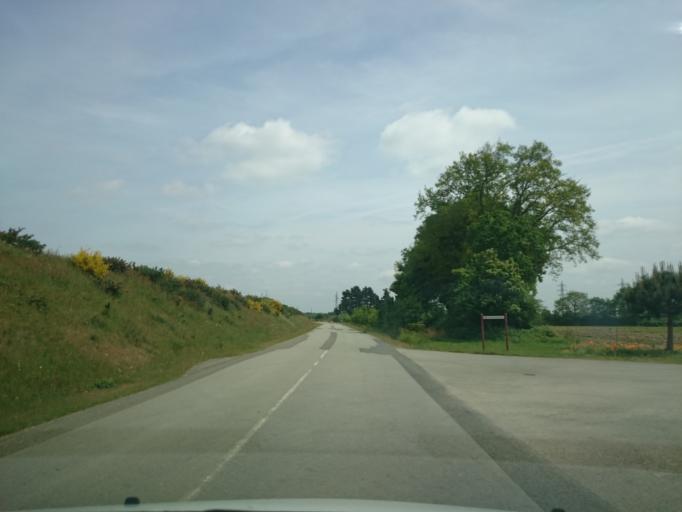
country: FR
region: Pays de la Loire
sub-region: Departement de la Loire-Atlantique
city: La Montagne
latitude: 47.1752
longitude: -1.6982
